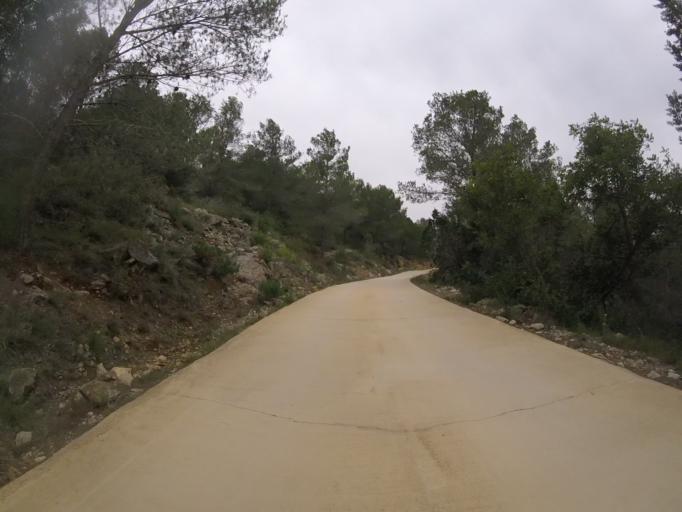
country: ES
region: Valencia
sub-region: Provincia de Castello
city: Alcala de Xivert
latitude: 40.3019
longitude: 0.2573
